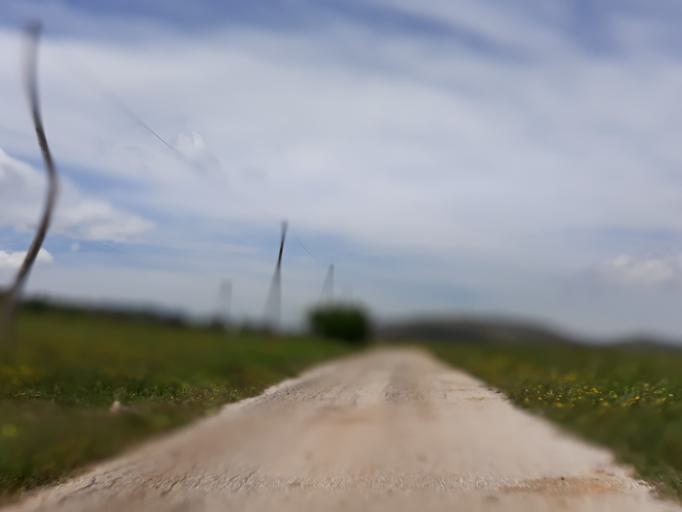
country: GR
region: Central Greece
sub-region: Nomos Voiotias
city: Ayios Thomas
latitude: 38.1817
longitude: 23.5576
